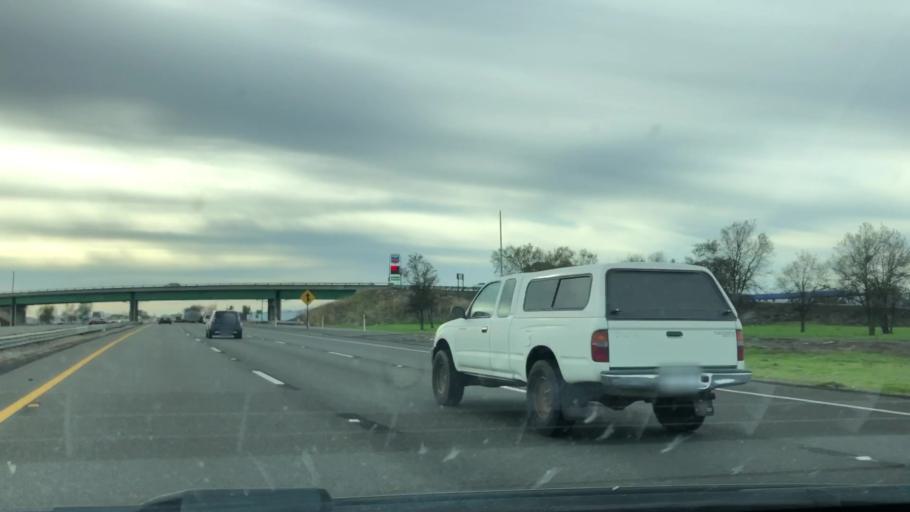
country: US
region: California
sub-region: Solano County
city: Dixon
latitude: 38.4916
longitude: -121.8022
